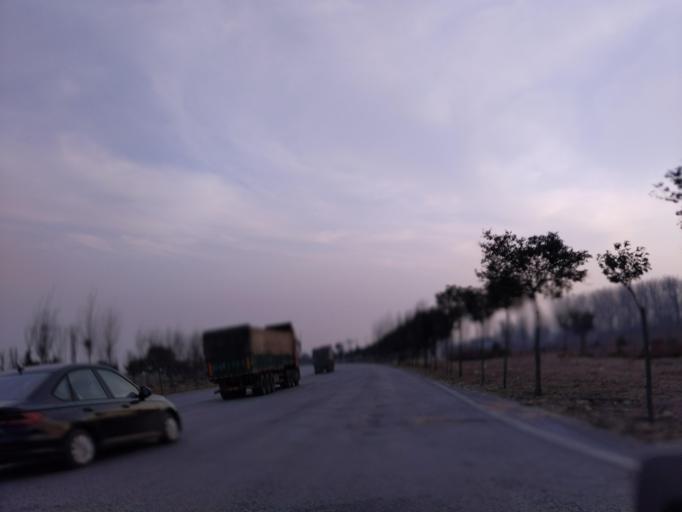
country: CN
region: Henan Sheng
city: Puyang
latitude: 35.8146
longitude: 114.9675
